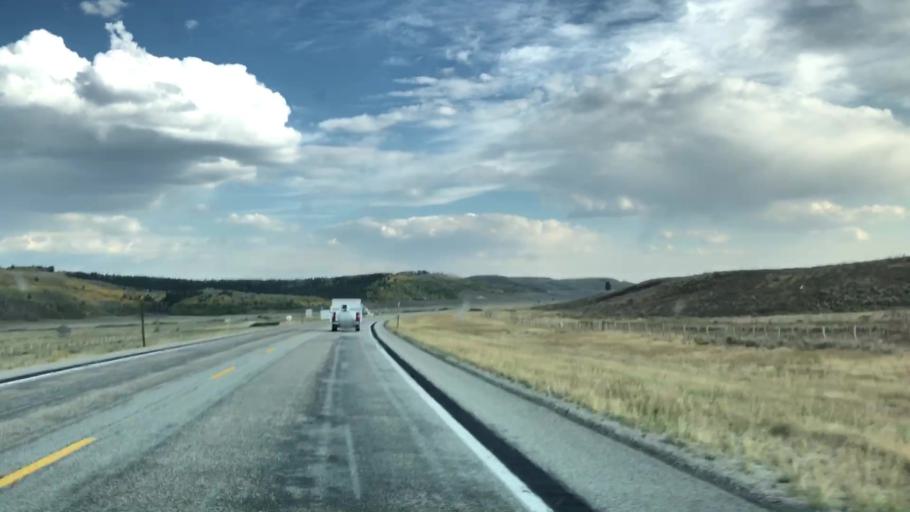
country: US
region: Wyoming
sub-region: Sublette County
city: Pinedale
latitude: 43.1181
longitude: -110.1785
